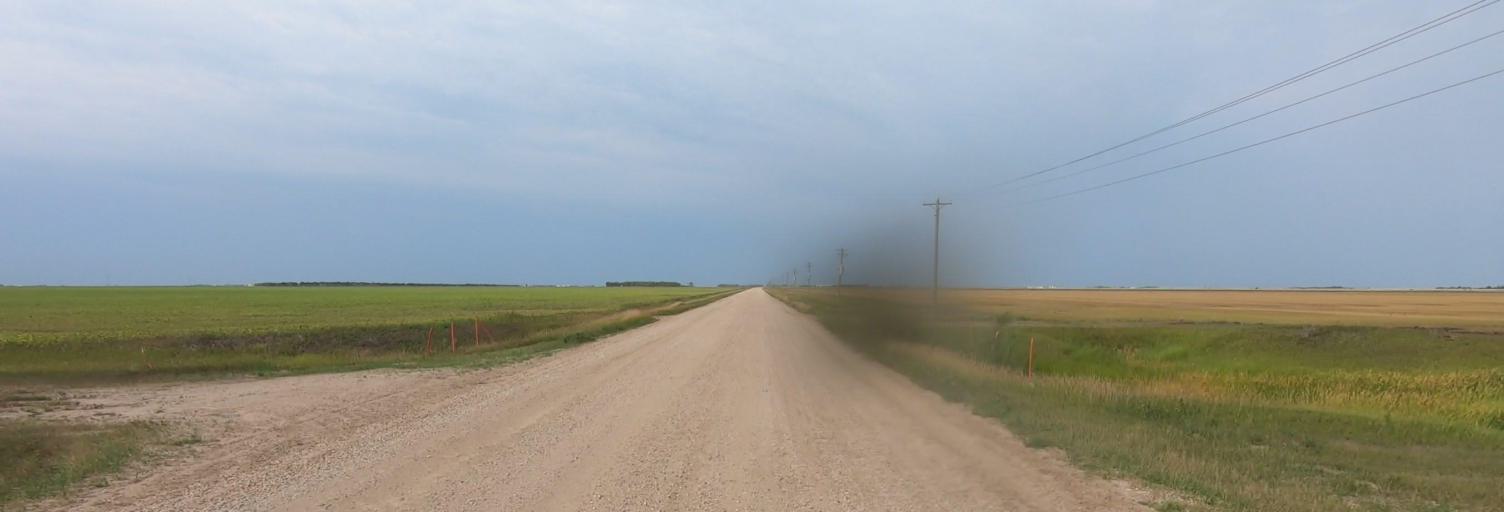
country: CA
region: Manitoba
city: Morris
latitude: 49.5750
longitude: -97.2858
